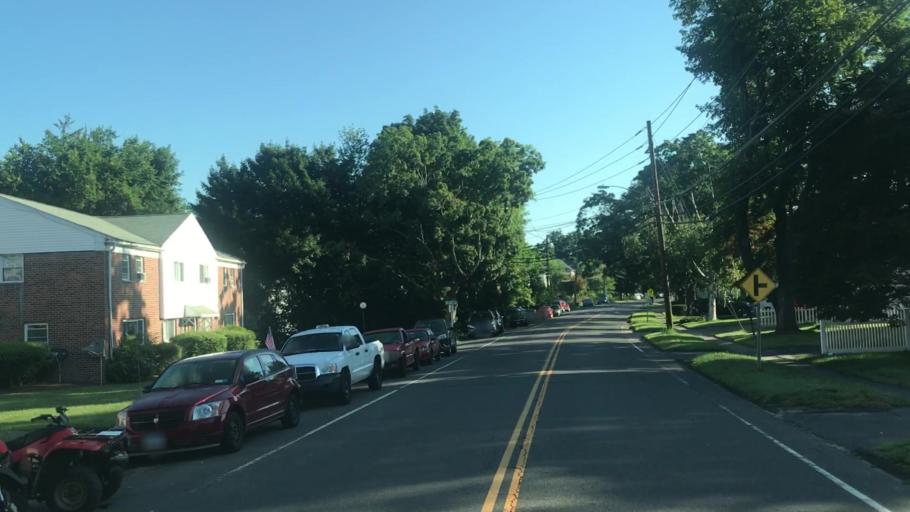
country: US
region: Connecticut
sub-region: Fairfield County
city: Danbury
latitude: 41.3871
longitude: -73.4628
